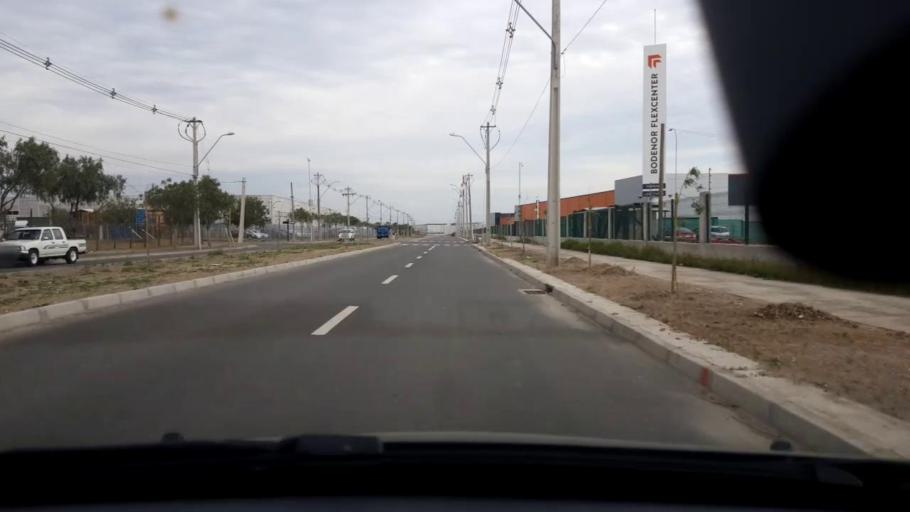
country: CL
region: Santiago Metropolitan
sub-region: Provincia de Santiago
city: Lo Prado
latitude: -33.4285
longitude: -70.7876
